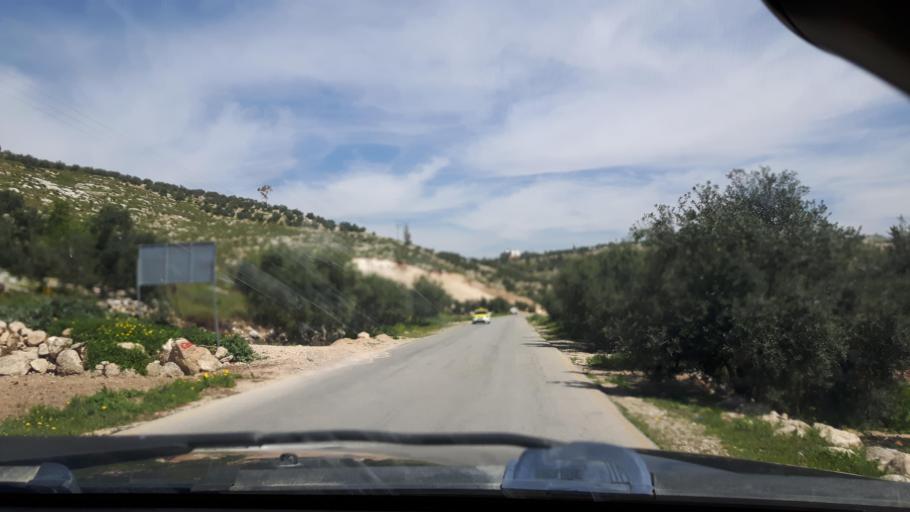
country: PS
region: West Bank
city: Kharbatha al Misbah
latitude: 31.8789
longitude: 35.0751
